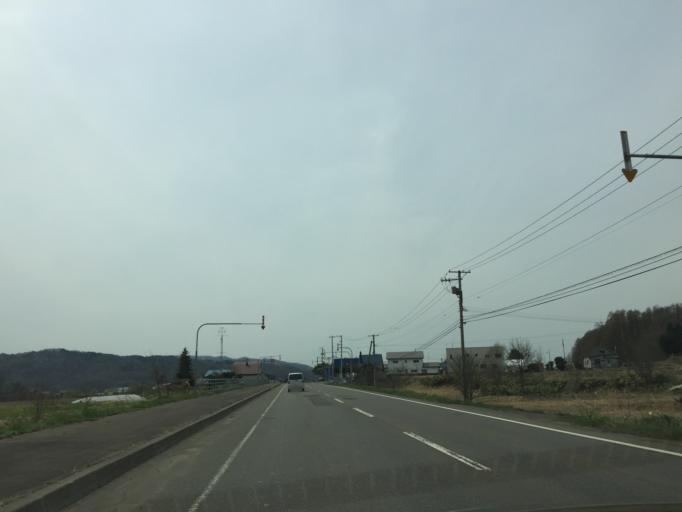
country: JP
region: Hokkaido
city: Ashibetsu
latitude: 43.5477
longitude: 142.1683
